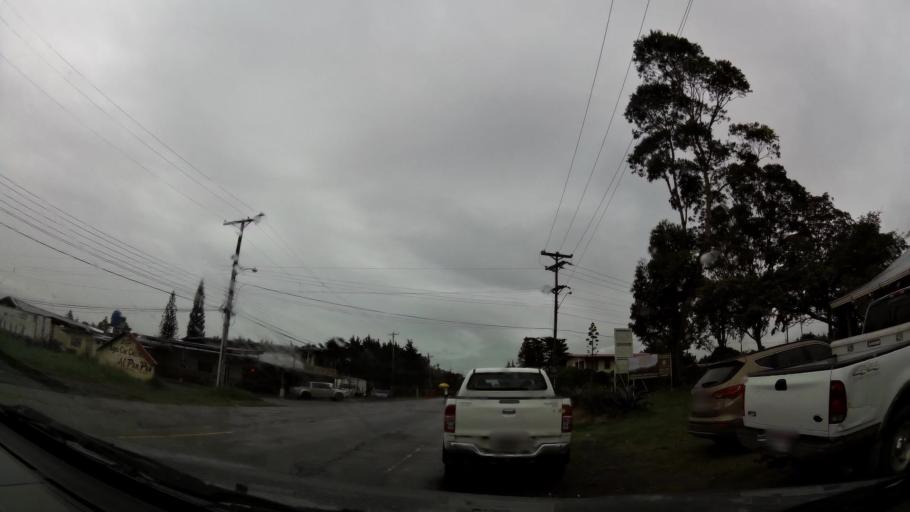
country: PA
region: Chiriqui
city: Volcan
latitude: 8.7723
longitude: -82.6357
